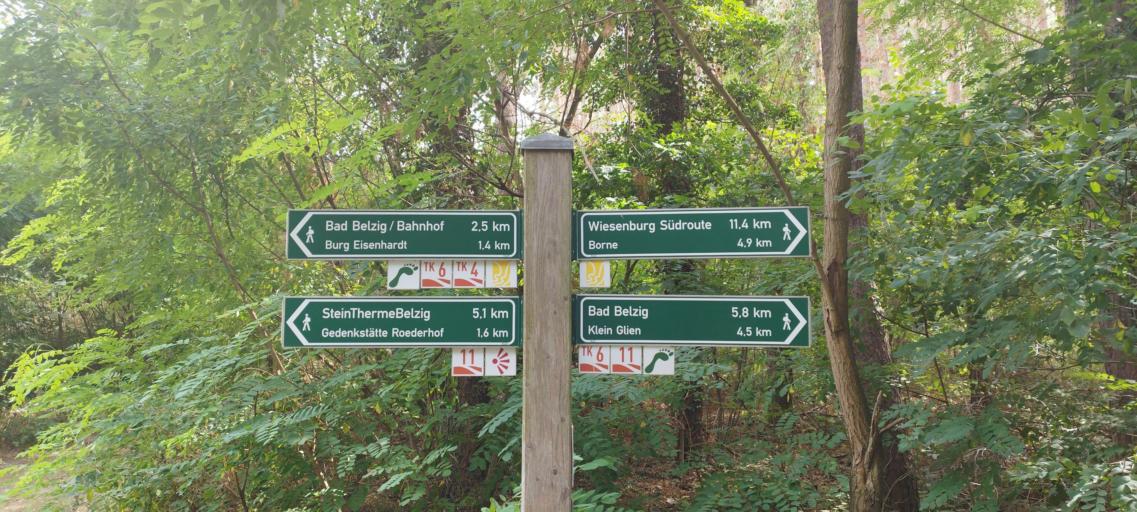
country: DE
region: Brandenburg
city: Belzig
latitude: 52.1336
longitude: 12.5681
